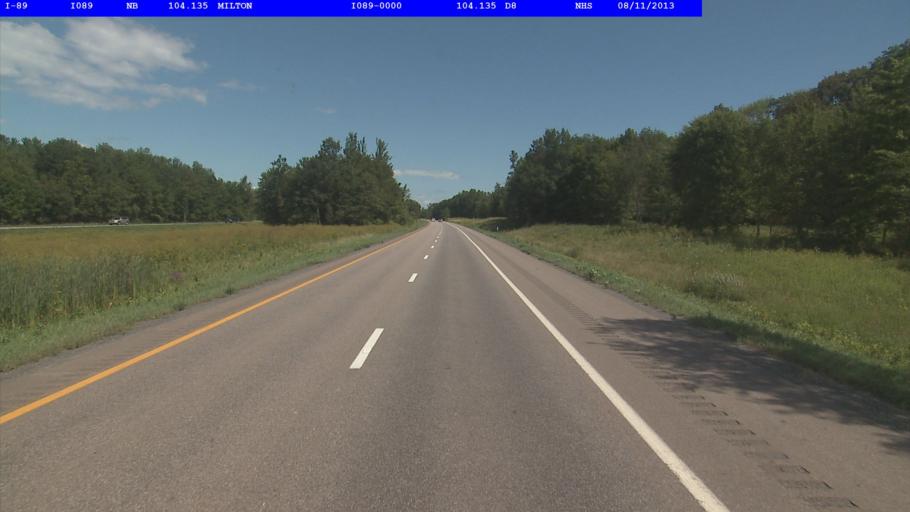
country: US
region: Vermont
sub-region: Chittenden County
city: Milton
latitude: 44.6723
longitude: -73.1320
